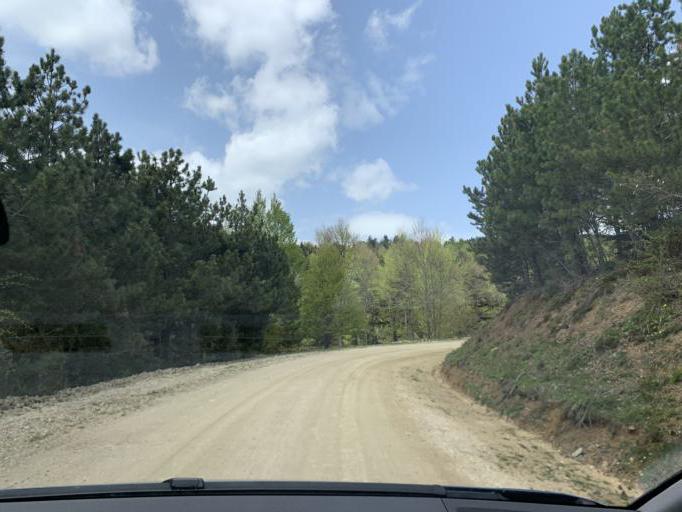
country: TR
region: Bolu
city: Bolu
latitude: 40.8345
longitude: 31.6700
